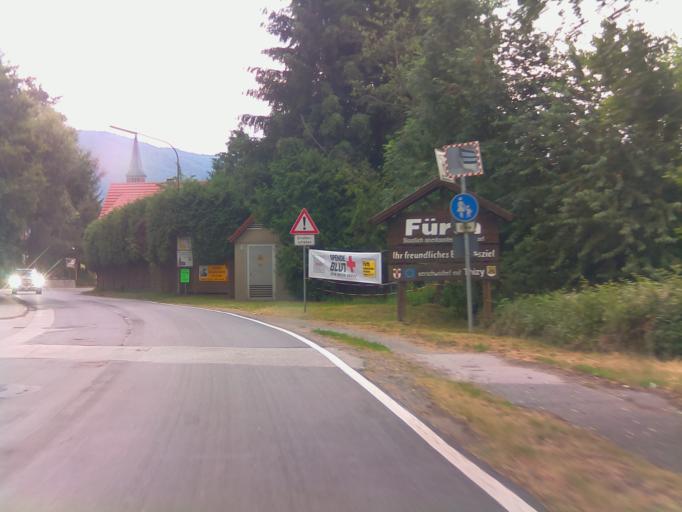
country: DE
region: Hesse
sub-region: Regierungsbezirk Darmstadt
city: Furth
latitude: 49.6530
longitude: 8.7751
